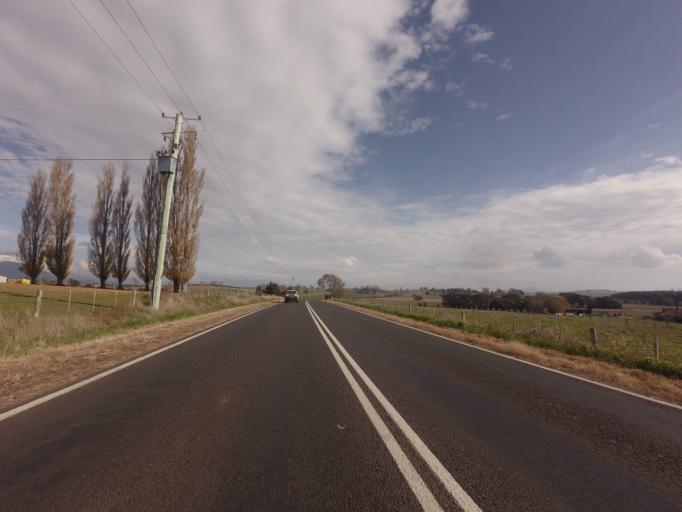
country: AU
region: Tasmania
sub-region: Meander Valley
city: Deloraine
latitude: -41.5221
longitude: 146.7189
